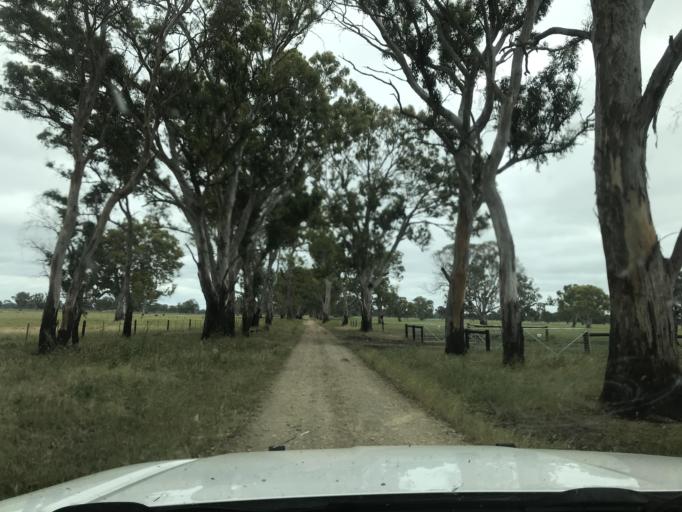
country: AU
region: South Australia
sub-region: Wattle Range
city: Penola
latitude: -37.1784
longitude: 141.0526
